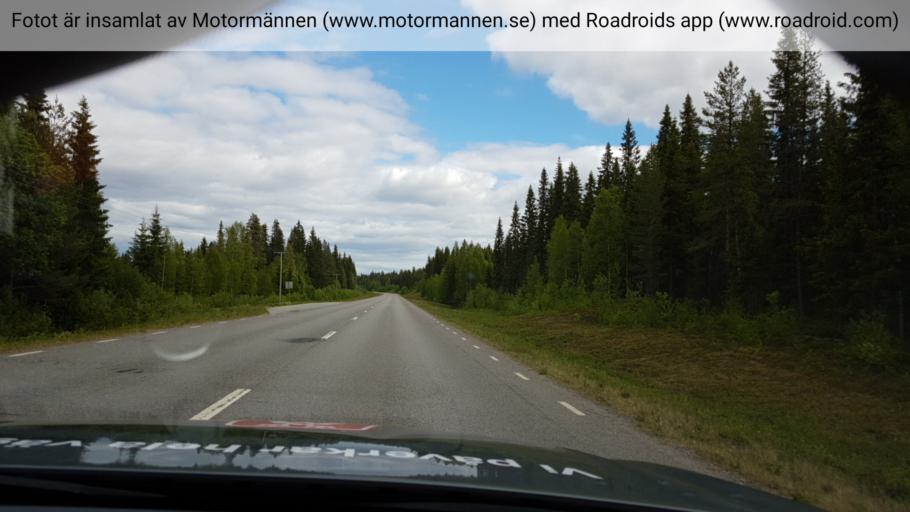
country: SE
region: Jaemtland
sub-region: Stroemsunds Kommun
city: Stroemsund
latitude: 64.2285
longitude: 15.4981
